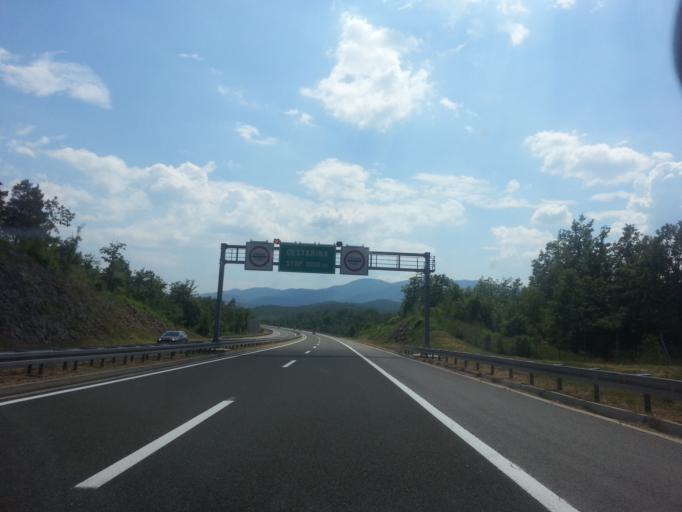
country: HR
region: Primorsko-Goranska
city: Klana
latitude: 45.4655
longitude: 14.2705
